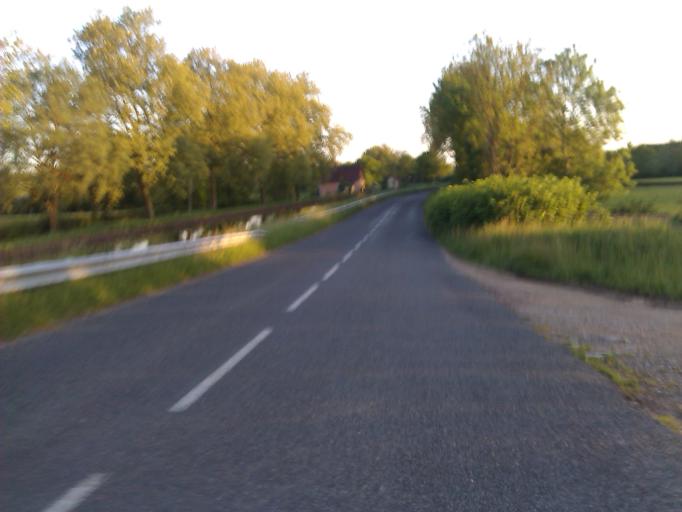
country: FR
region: Bourgogne
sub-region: Departement de Saone-et-Loire
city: Paray-le-Monial
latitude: 46.4693
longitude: 4.1660
